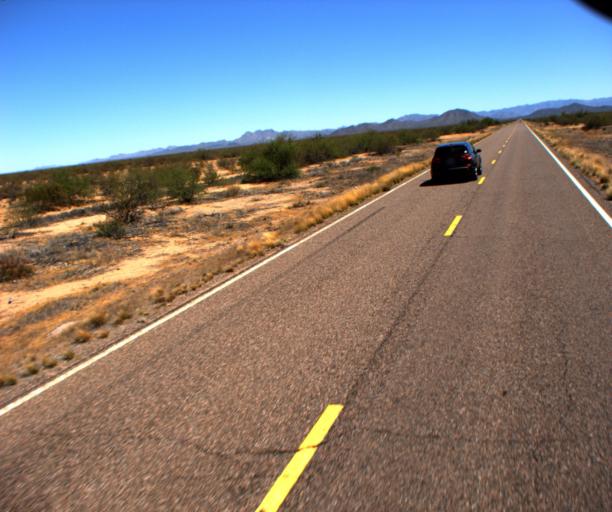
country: US
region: Arizona
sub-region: Yavapai County
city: Congress
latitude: 34.0392
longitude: -113.0725
